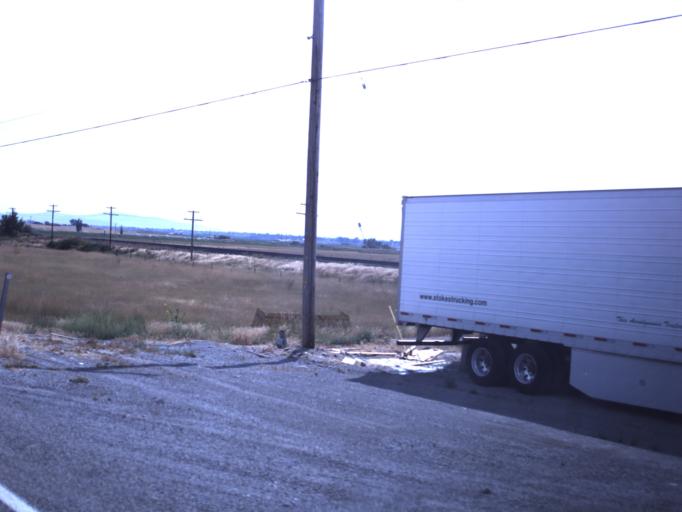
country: US
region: Utah
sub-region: Box Elder County
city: Garland
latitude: 41.7713
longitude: -112.0966
